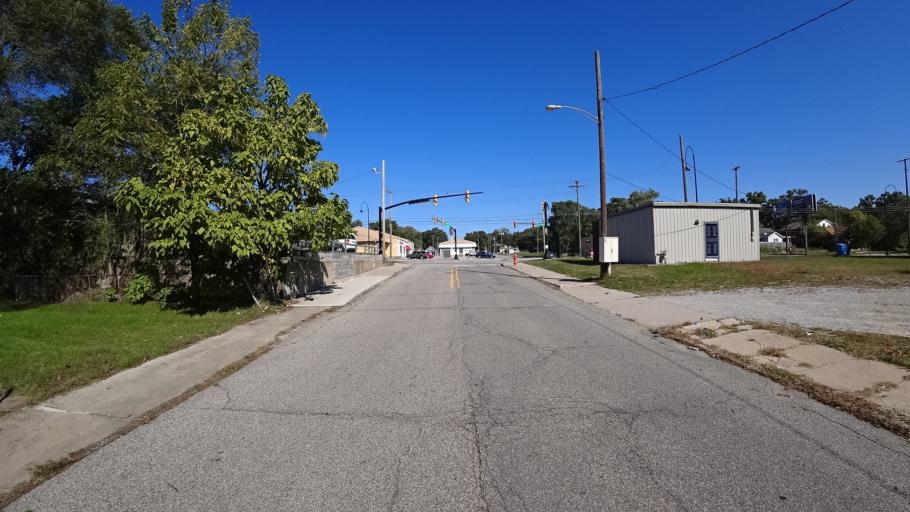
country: US
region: Indiana
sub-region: LaPorte County
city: Michigan City
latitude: 41.7114
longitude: -86.8820
